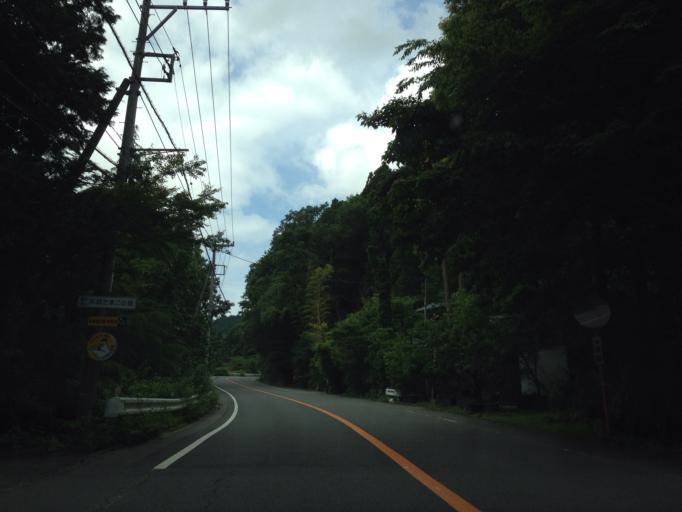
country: JP
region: Shizuoka
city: Heda
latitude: 34.9191
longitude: 138.8701
